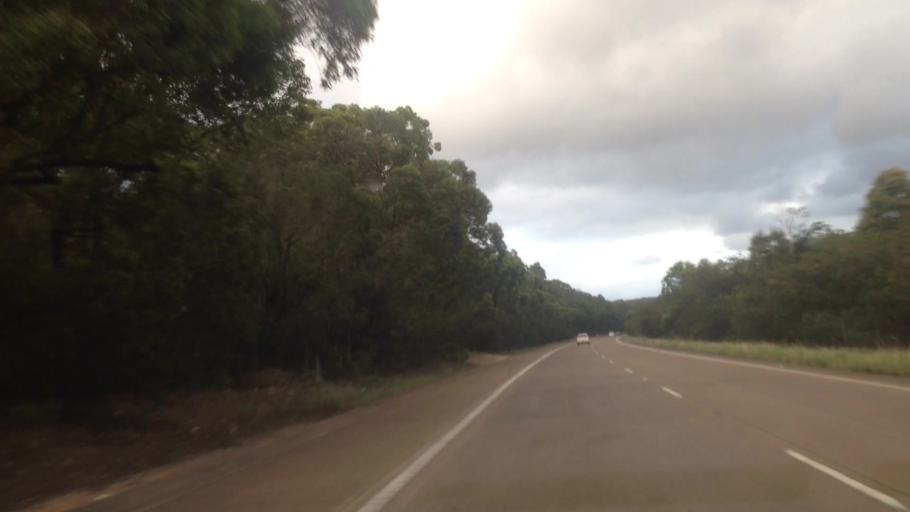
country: AU
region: New South Wales
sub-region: Wyong Shire
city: Charmhaven
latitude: -33.1722
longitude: 151.4668
